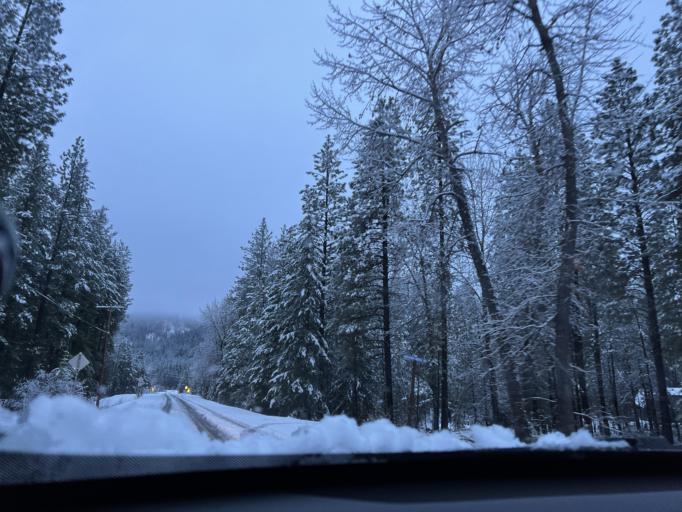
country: US
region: Washington
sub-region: Chelan County
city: Granite Falls
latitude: 48.5917
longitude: -120.4056
